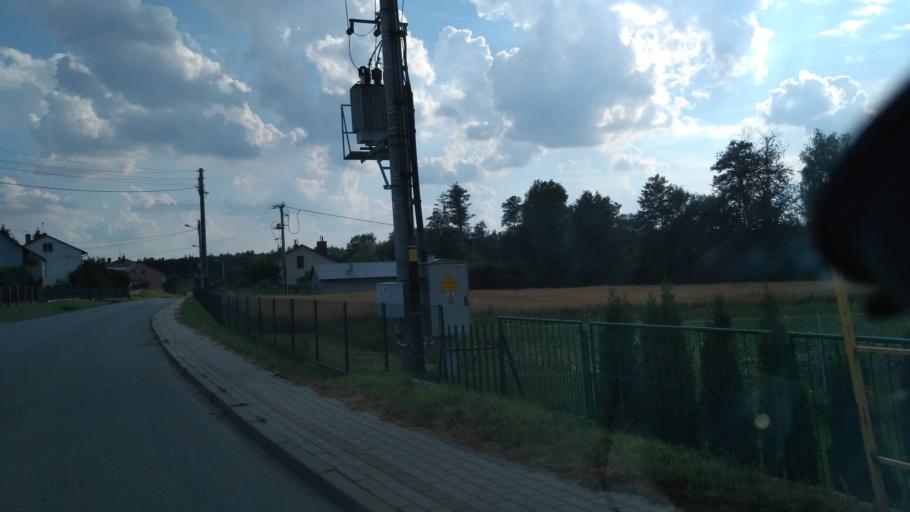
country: PL
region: Subcarpathian Voivodeship
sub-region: Powiat rzeszowski
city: Wysoka Glogowska
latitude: 50.1551
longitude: 22.0208
